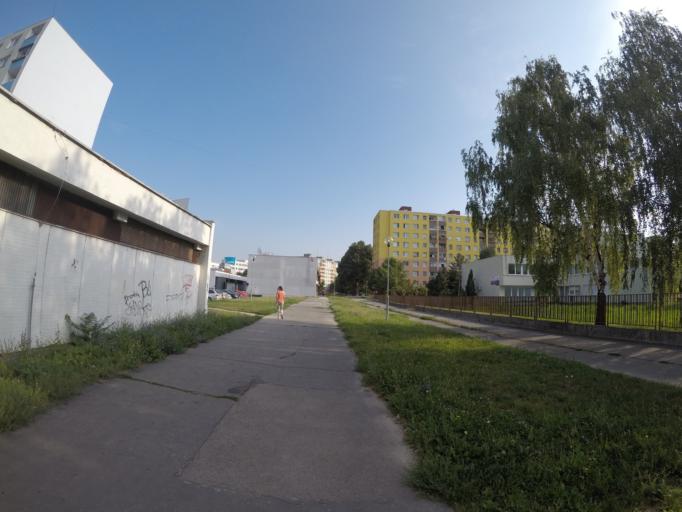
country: SK
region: Bratislavsky
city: Bratislava
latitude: 48.1189
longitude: 17.1020
